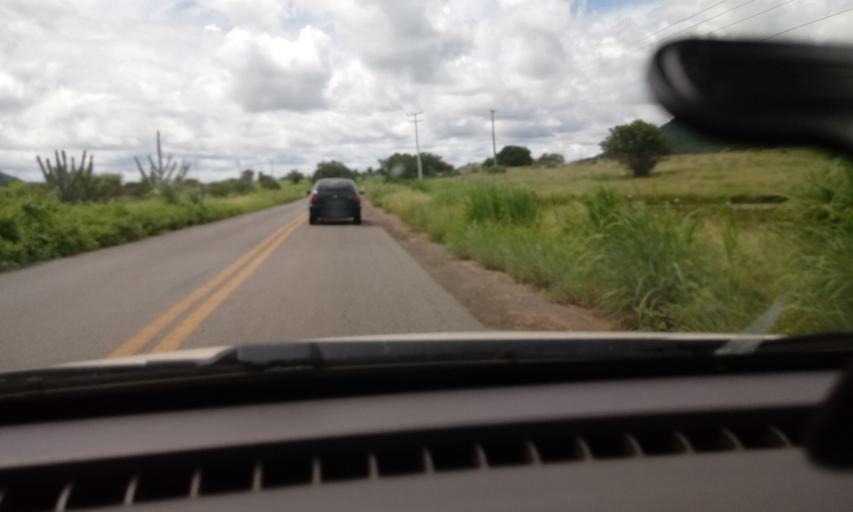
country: BR
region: Bahia
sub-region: Guanambi
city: Guanambi
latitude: -14.0947
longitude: -42.8724
